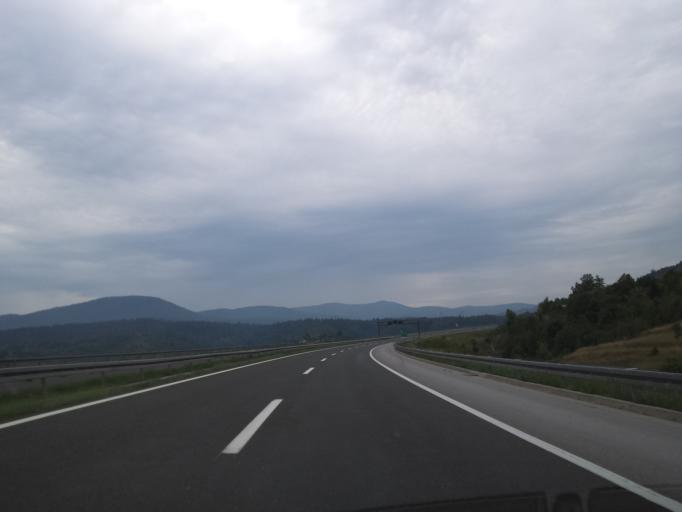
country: HR
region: Karlovacka
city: Ostarije
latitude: 45.1435
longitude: 15.2724
